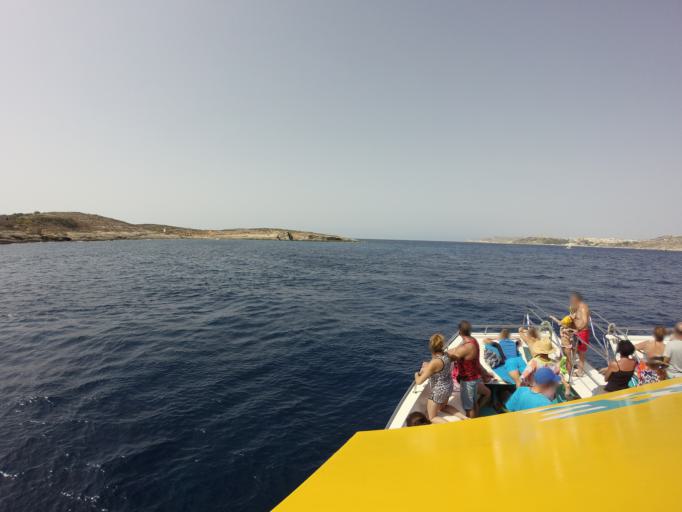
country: MT
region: Il-Qala
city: Qala
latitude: 36.0203
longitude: 14.3274
